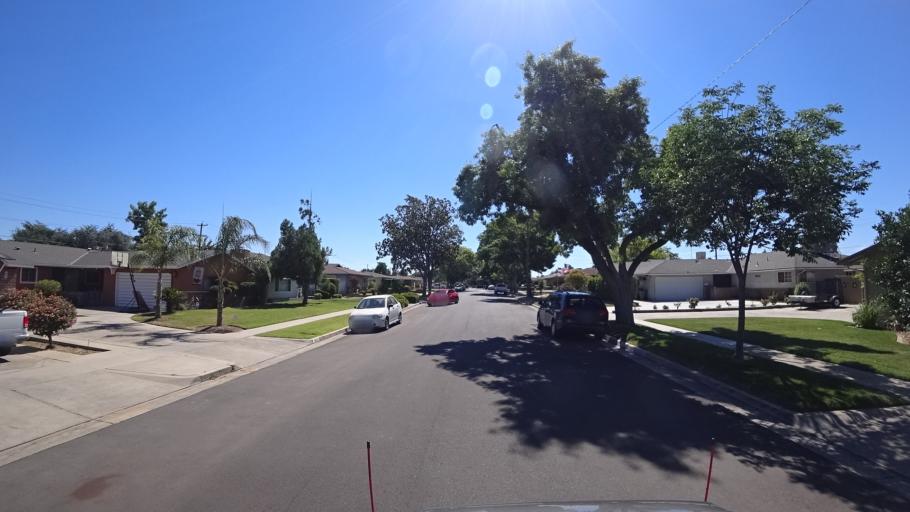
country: US
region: California
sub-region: Fresno County
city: Fresno
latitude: 36.7843
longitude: -119.8335
